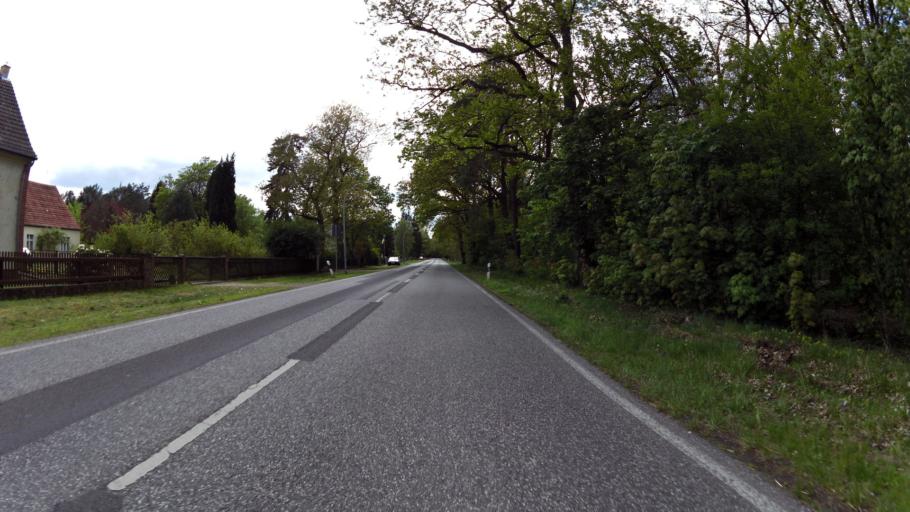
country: DE
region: Brandenburg
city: Rauen
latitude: 52.3556
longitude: 14.0177
